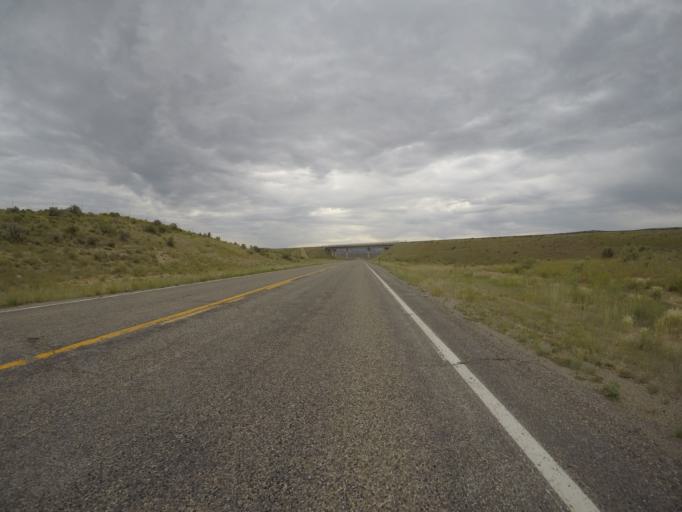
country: US
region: Wyoming
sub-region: Lincoln County
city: Kemmerer
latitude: 41.8219
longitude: -110.7320
